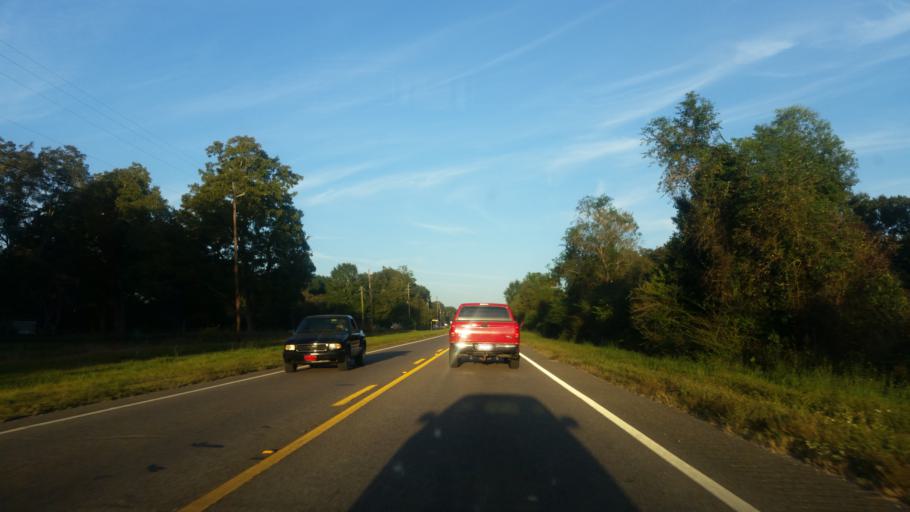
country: US
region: Alabama
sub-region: Mobile County
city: Grand Bay
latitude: 30.4716
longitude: -88.3624
